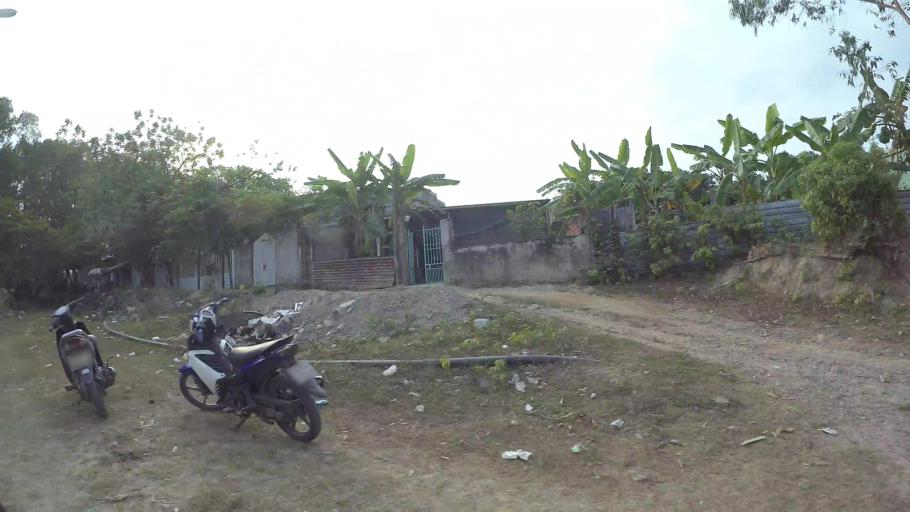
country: VN
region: Da Nang
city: Lien Chieu
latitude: 16.0488
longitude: 108.1530
